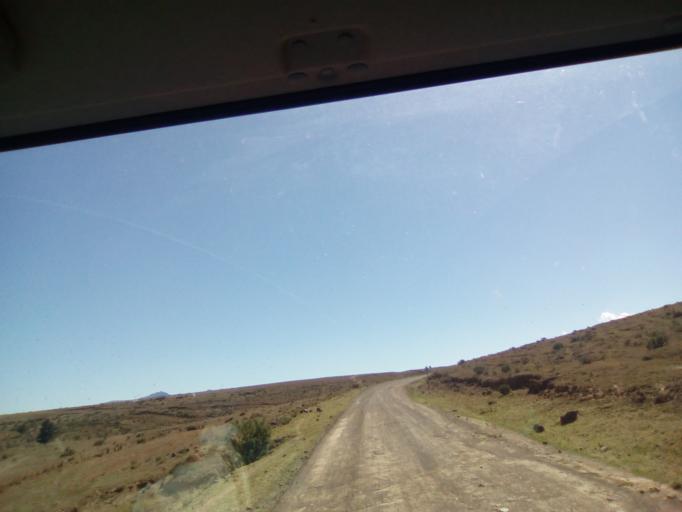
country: LS
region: Qacha's Nek
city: Qacha's Nek
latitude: -30.0341
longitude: 28.6632
